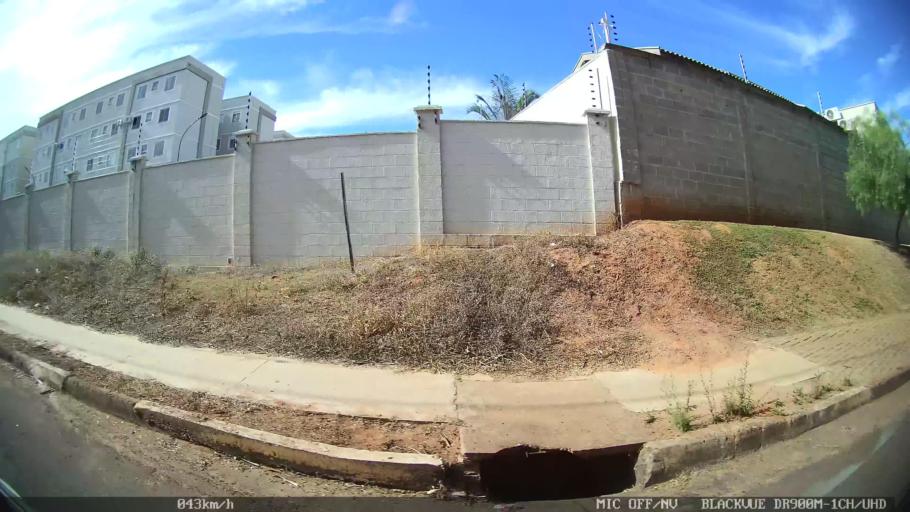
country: BR
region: Sao Paulo
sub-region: Catanduva
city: Catanduva
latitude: -21.1229
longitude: -48.9591
